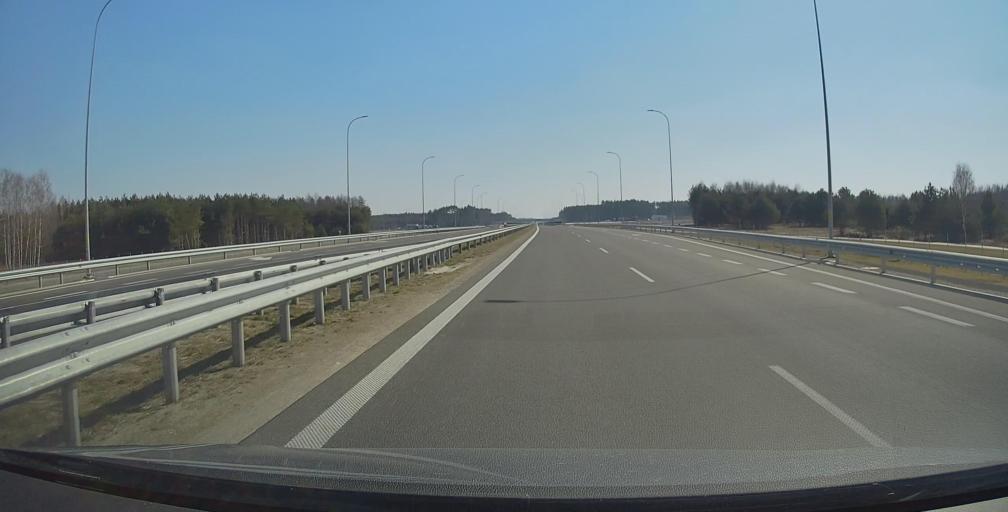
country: PL
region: Subcarpathian Voivodeship
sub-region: Powiat nizanski
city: Jezowe
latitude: 50.3905
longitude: 22.1504
